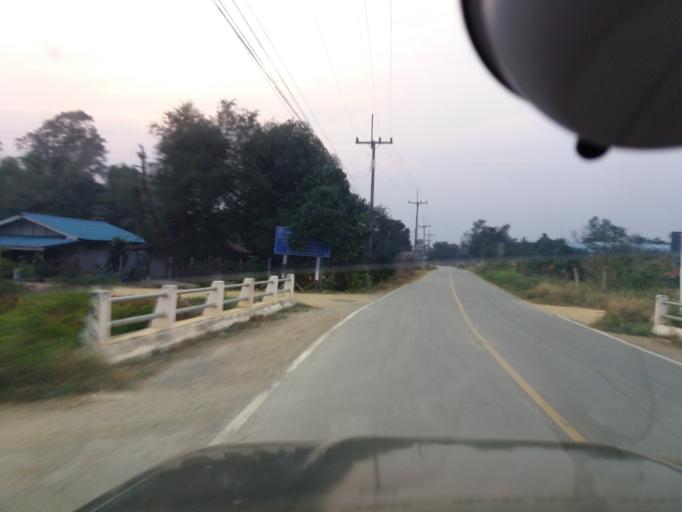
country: TH
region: Suphan Buri
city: Doem Bang Nang Buat
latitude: 14.8921
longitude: 100.1660
